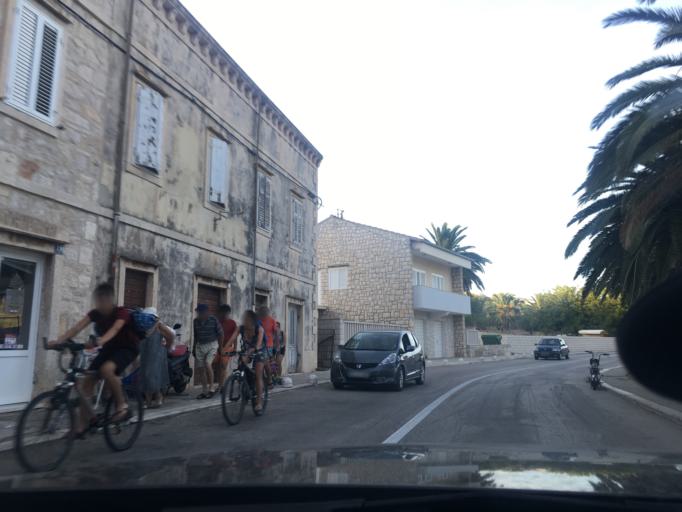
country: HR
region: Splitsko-Dalmatinska
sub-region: Grad Vis
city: Vis
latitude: 43.0631
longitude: 16.1846
